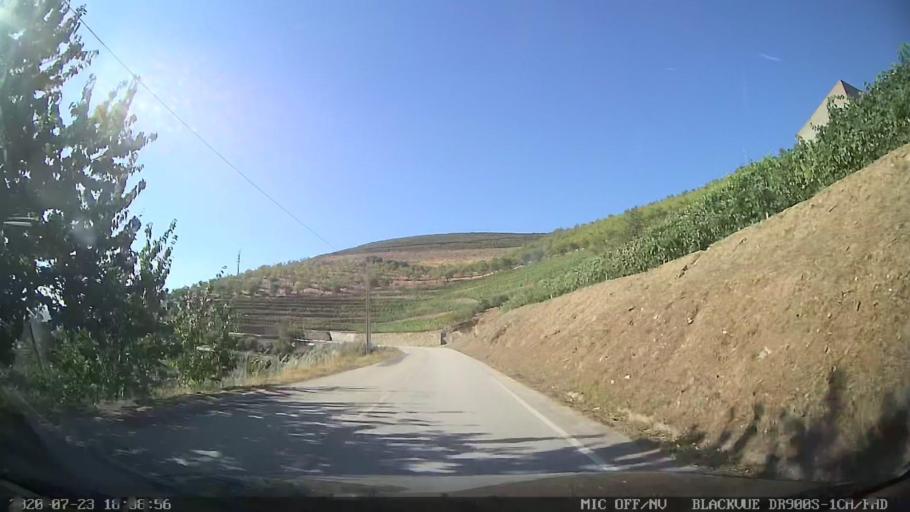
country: PT
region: Viseu
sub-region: Sao Joao da Pesqueira
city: Sao Joao da Pesqueira
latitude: 41.1799
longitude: -7.4371
